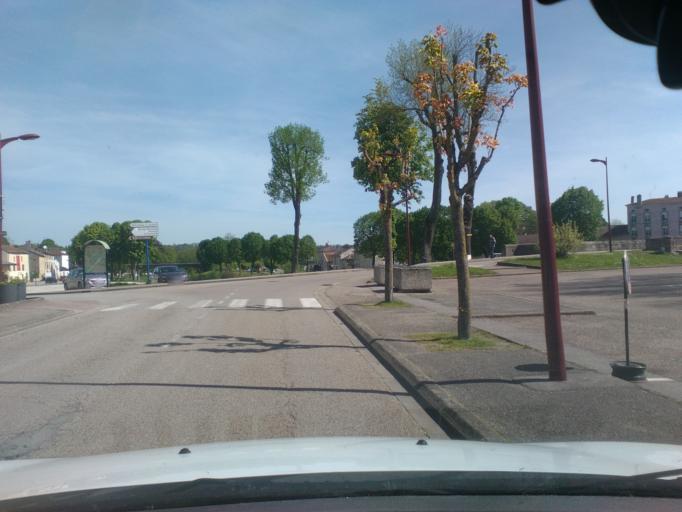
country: FR
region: Lorraine
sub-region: Departement des Vosges
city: Mirecourt
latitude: 48.3003
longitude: 6.1362
